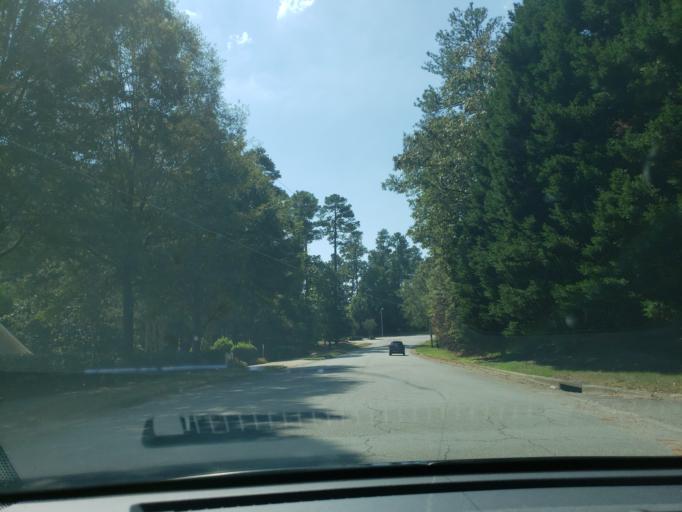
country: US
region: North Carolina
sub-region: Durham County
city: Durham
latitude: 35.9077
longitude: -78.9278
